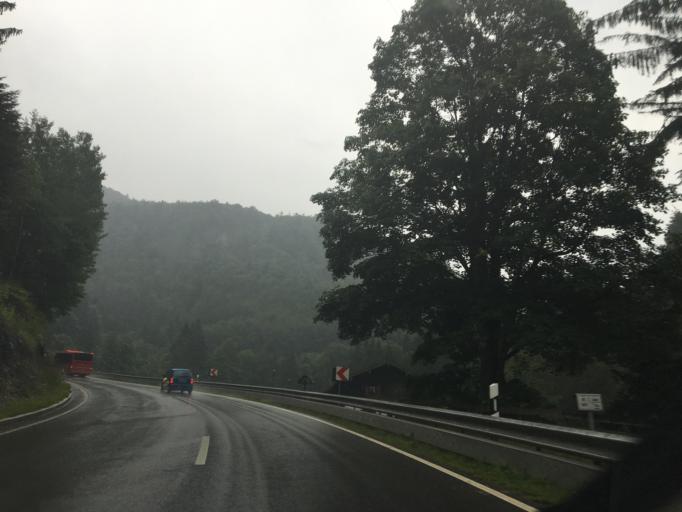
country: DE
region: Bavaria
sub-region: Upper Bavaria
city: Reit im Winkl
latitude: 47.6991
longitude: 12.4802
